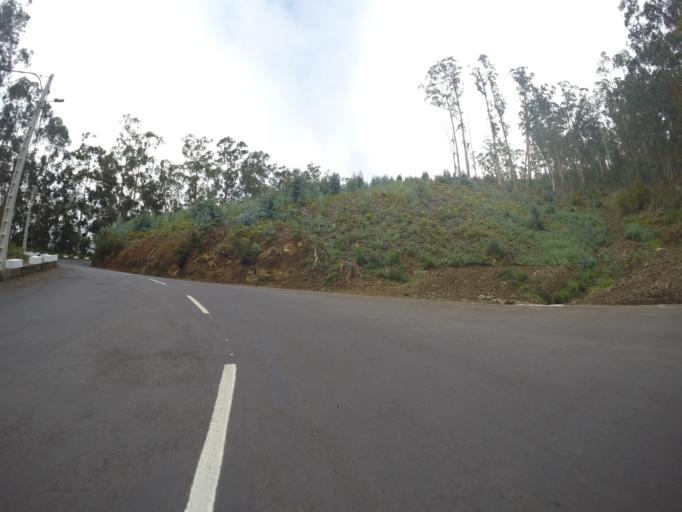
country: PT
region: Madeira
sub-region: Camara de Lobos
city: Curral das Freiras
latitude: 32.6908
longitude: -16.9550
